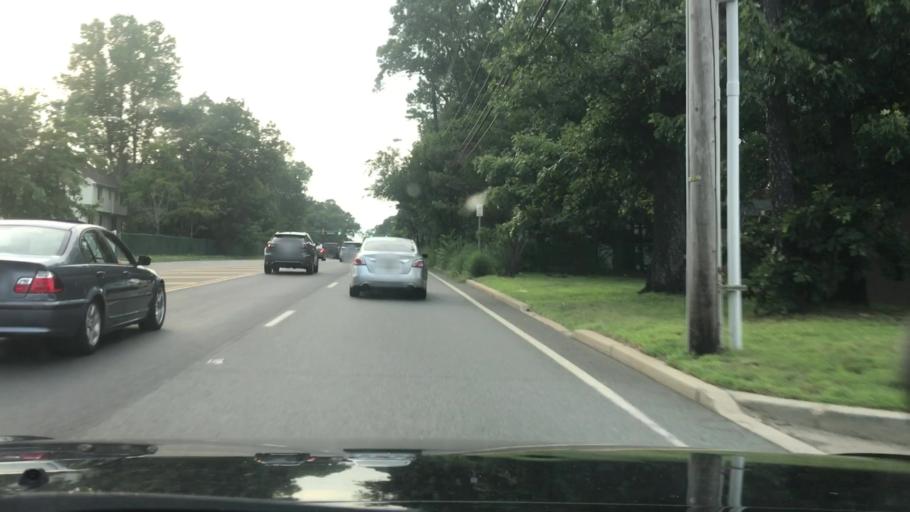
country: US
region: New Jersey
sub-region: Ocean County
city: Lakewood
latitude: 40.1099
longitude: -74.2372
